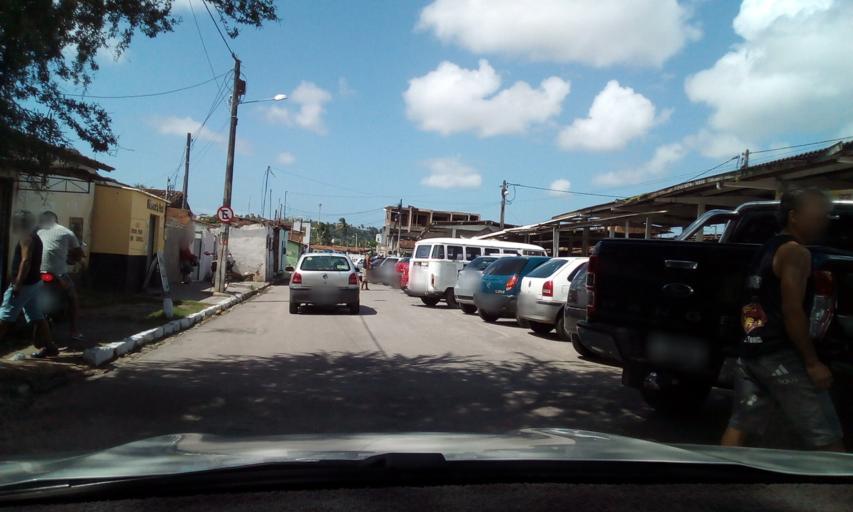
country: BR
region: Paraiba
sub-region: Bayeux
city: Bayeux
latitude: -7.1303
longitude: -34.9274
